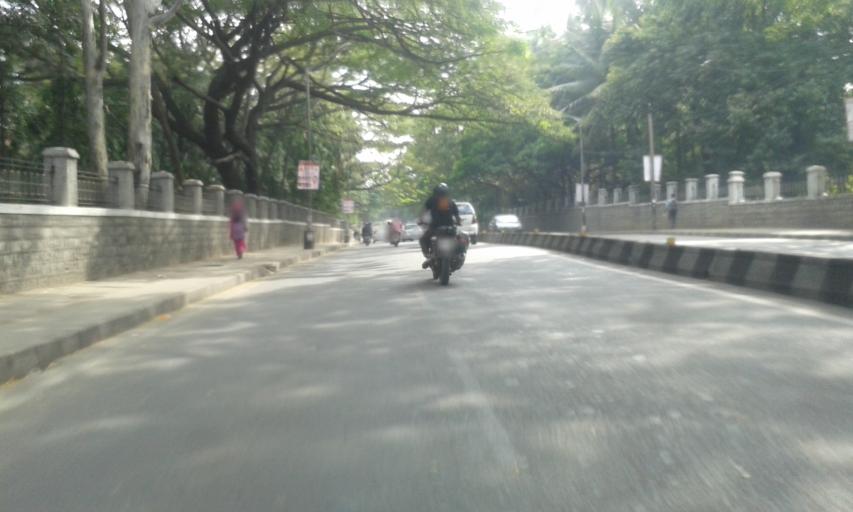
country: IN
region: Karnataka
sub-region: Bangalore Urban
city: Bangalore
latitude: 12.9426
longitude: 77.5974
